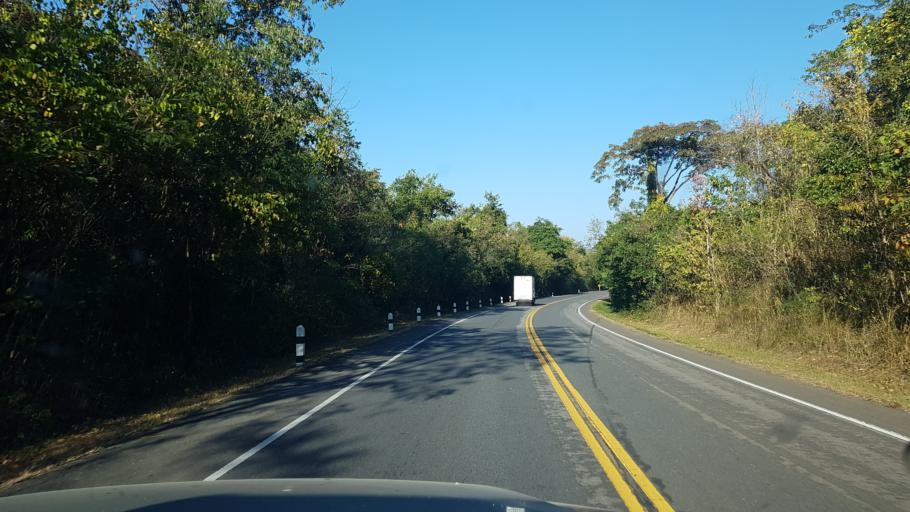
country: TH
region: Phetchabun
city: Nam Nao
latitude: 16.7570
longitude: 101.4640
